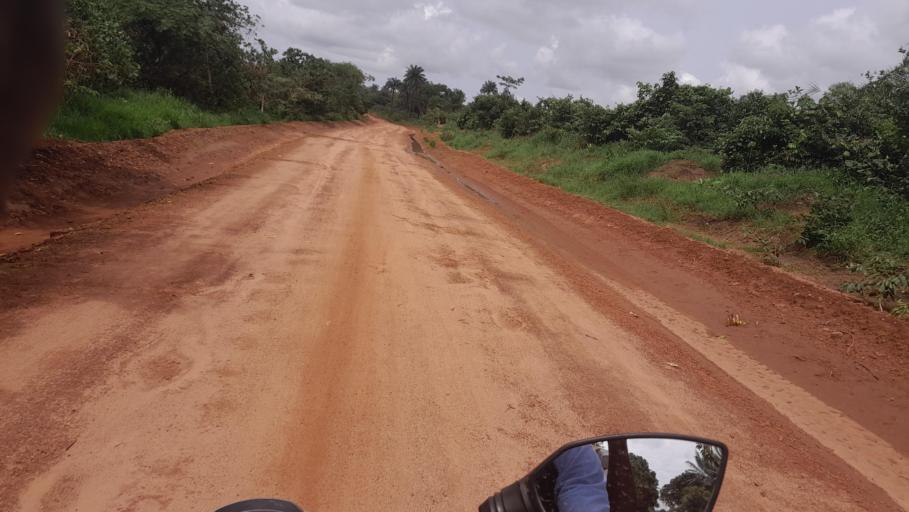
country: GN
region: Boke
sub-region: Boffa
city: Boffa
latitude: 10.0921
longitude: -13.8603
